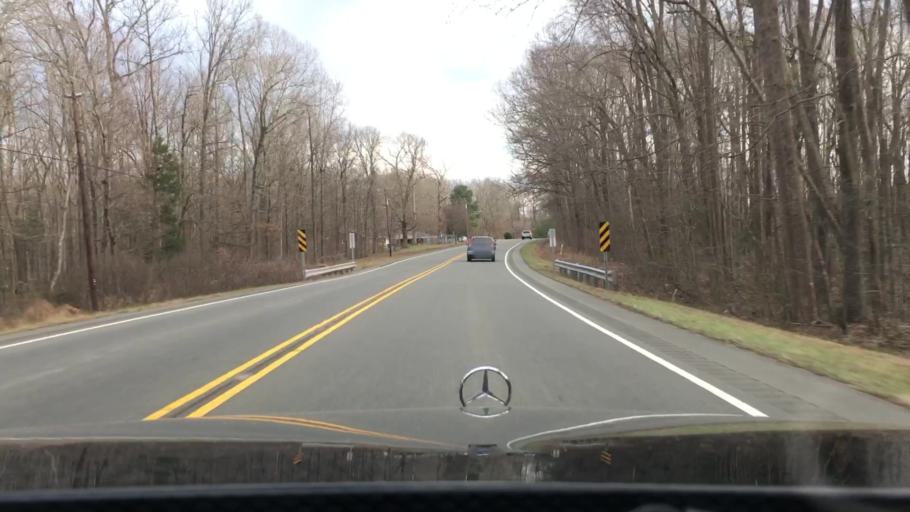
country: US
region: North Carolina
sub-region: Orange County
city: Hillsborough
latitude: 36.2015
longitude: -79.1452
